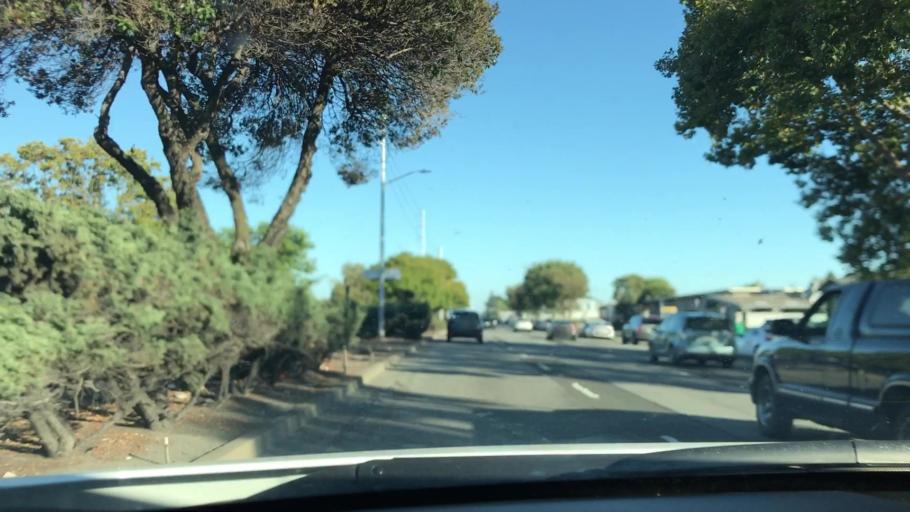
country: US
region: California
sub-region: Alameda County
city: San Lorenzo
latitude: 37.6776
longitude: -122.1257
